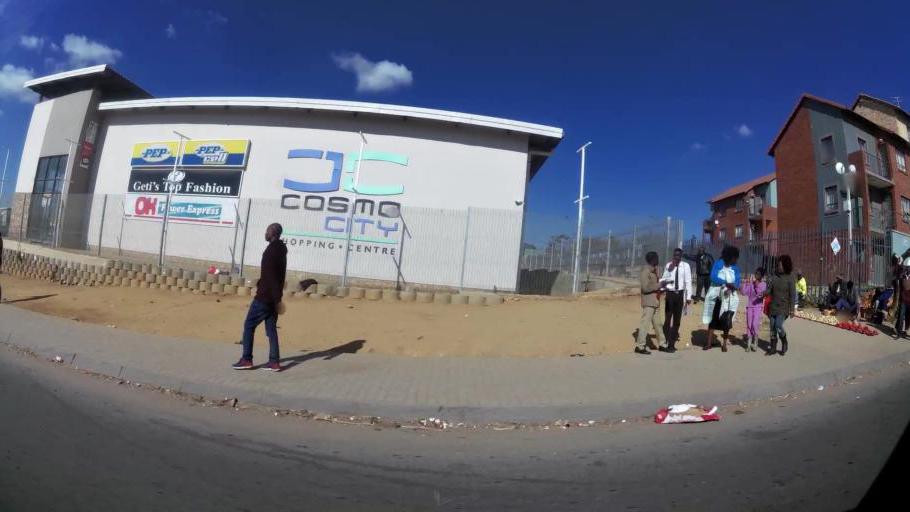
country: ZA
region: Gauteng
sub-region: West Rand District Municipality
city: Muldersdriseloop
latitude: -26.0211
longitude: 27.9272
